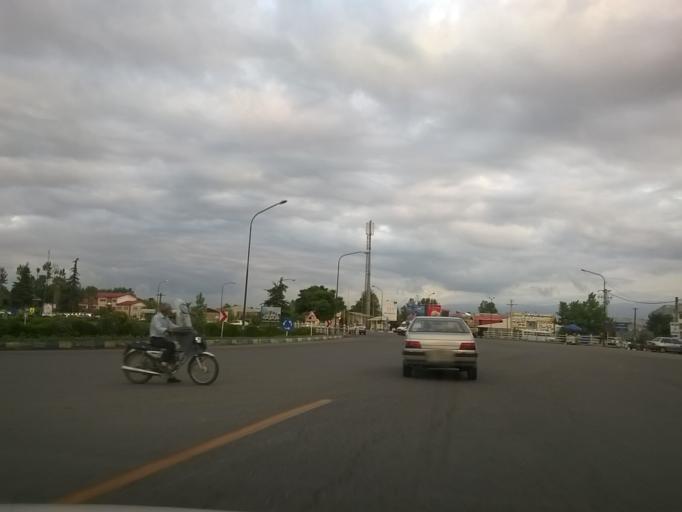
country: IR
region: Gilan
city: Astaneh-ye Ashrafiyeh
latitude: 37.2587
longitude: 49.9307
